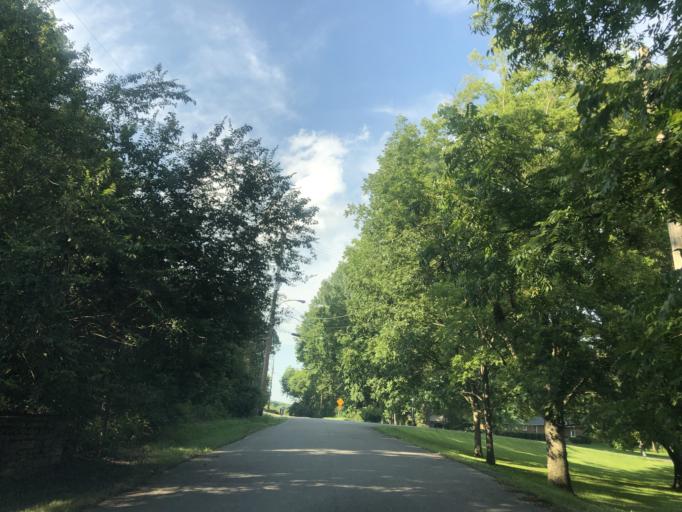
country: US
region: Tennessee
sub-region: Davidson County
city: Nashville
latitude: 36.2359
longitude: -86.8365
